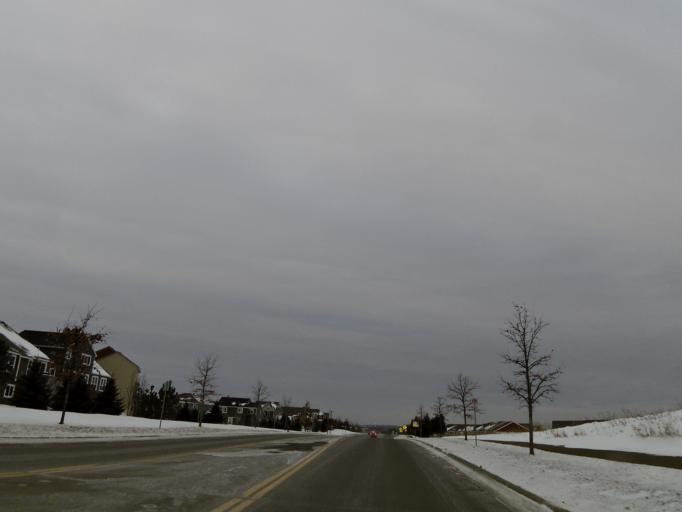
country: US
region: Minnesota
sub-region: Washington County
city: Afton
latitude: 44.9020
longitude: -92.8661
